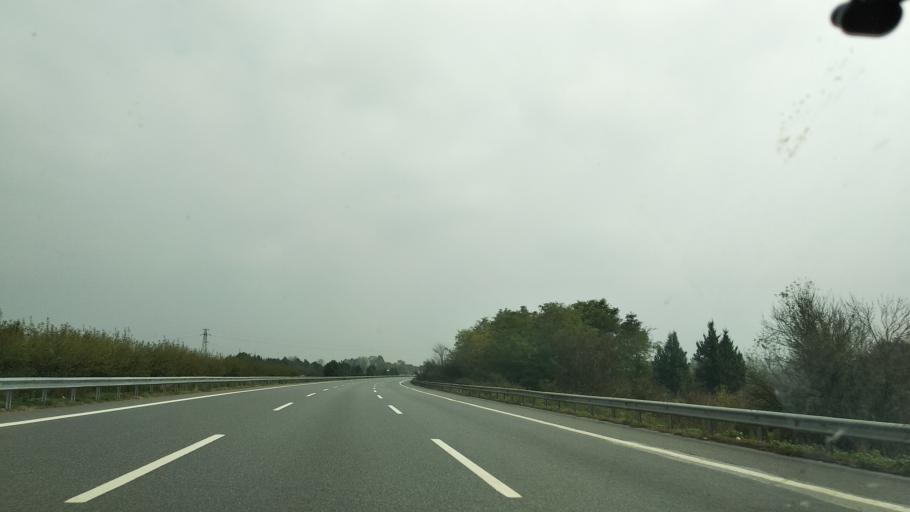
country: TR
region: Duzce
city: Cilimli
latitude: 40.8446
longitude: 31.0152
